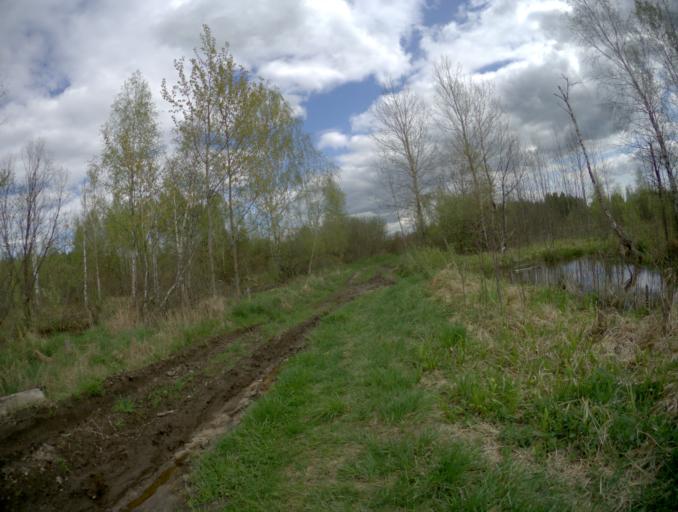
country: RU
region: Vladimir
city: Golovino
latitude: 55.9418
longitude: 40.4201
